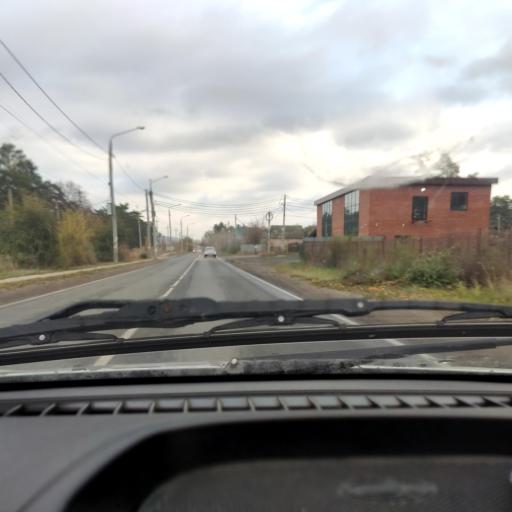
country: RU
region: Samara
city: Zhigulevsk
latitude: 53.4653
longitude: 49.6028
